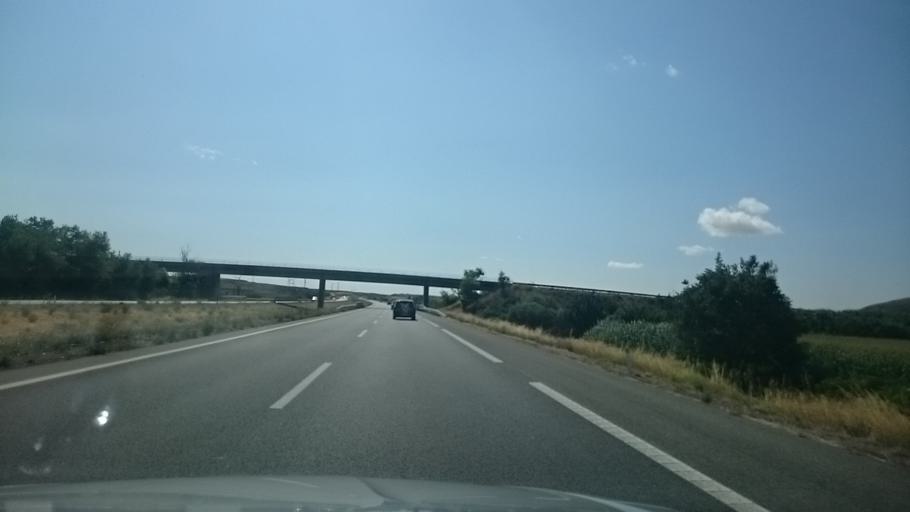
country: ES
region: Aragon
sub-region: Provincia de Zaragoza
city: Mallen
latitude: 41.8931
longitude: -1.4309
